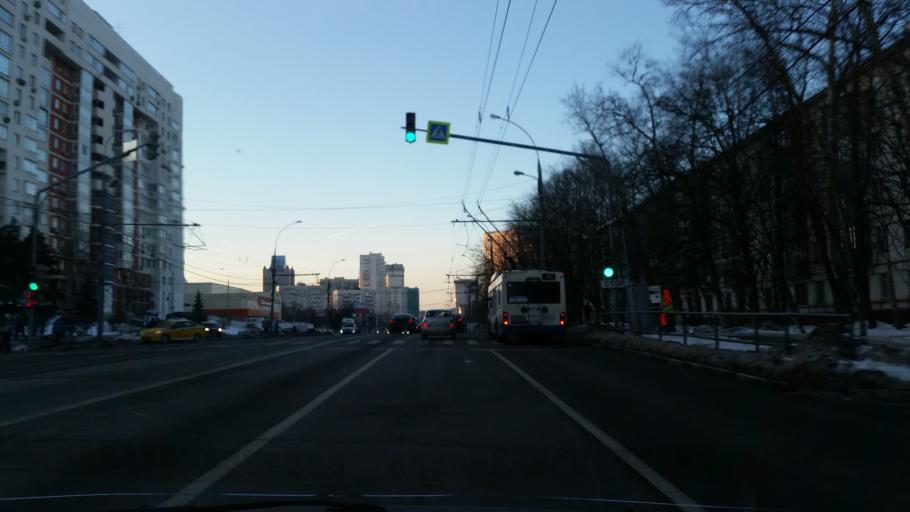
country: RU
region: Moscow
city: Zyuzino
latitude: 55.6550
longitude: 37.5760
